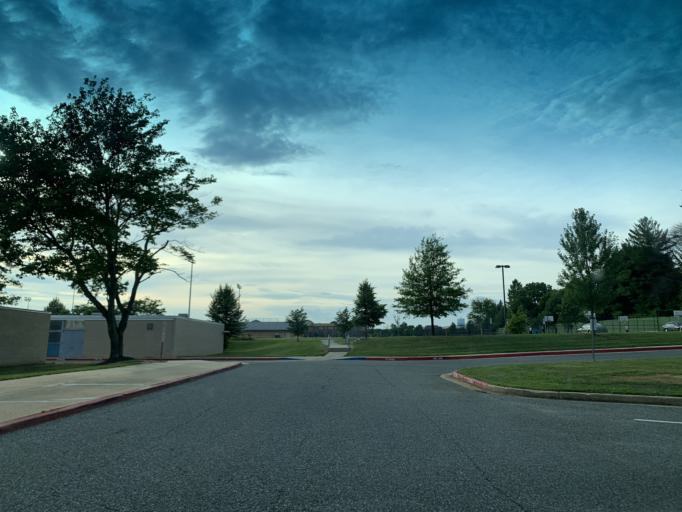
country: US
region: Maryland
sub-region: Harford County
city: South Bel Air
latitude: 39.5279
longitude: -76.3441
